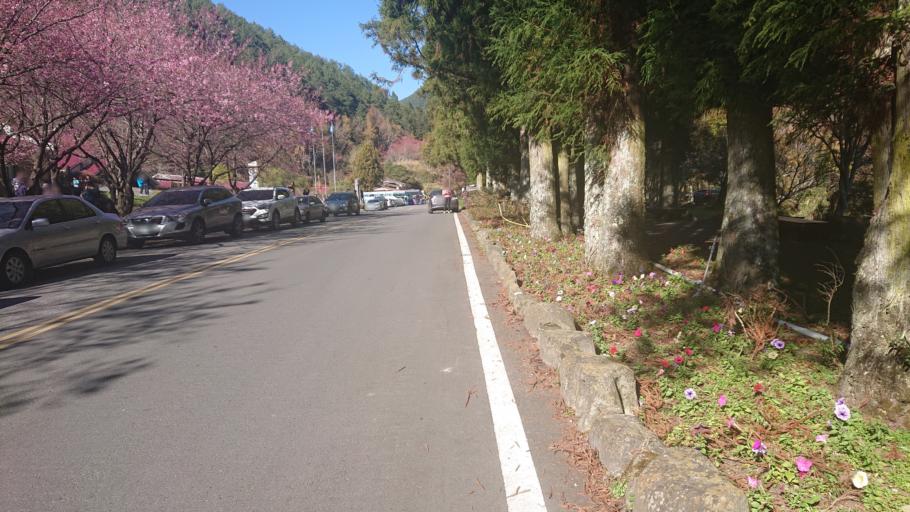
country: TW
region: Taiwan
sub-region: Hualien
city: Hualian
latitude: 24.3522
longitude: 121.3098
